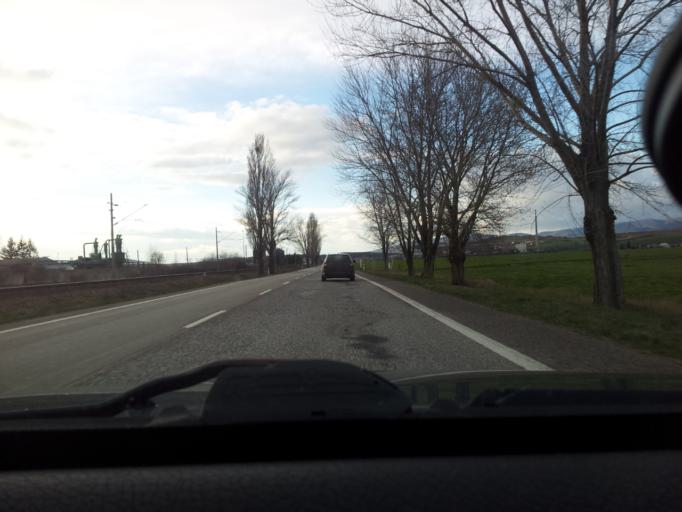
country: SK
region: Nitriansky
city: Tlmace
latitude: 48.2742
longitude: 18.5563
